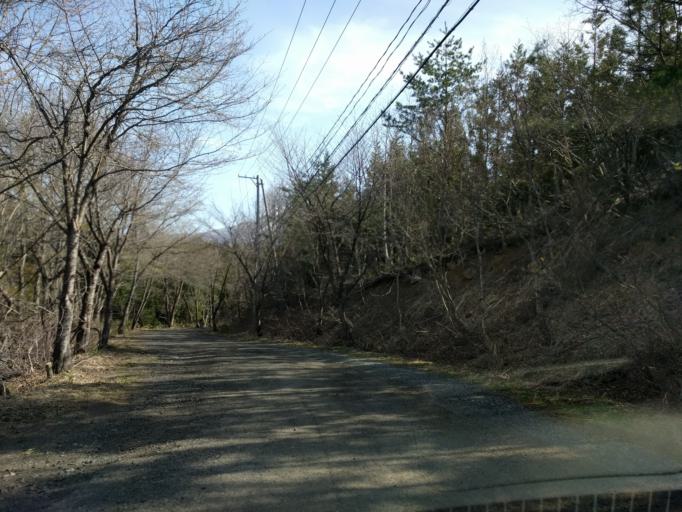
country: JP
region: Fukushima
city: Inawashiro
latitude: 37.5249
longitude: 140.0360
